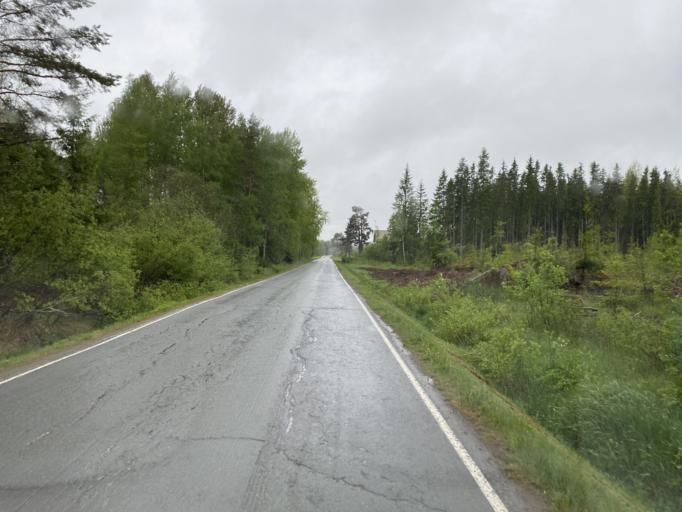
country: FI
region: Pirkanmaa
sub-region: Etelae-Pirkanmaa
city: Urjala
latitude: 60.9671
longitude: 23.5225
